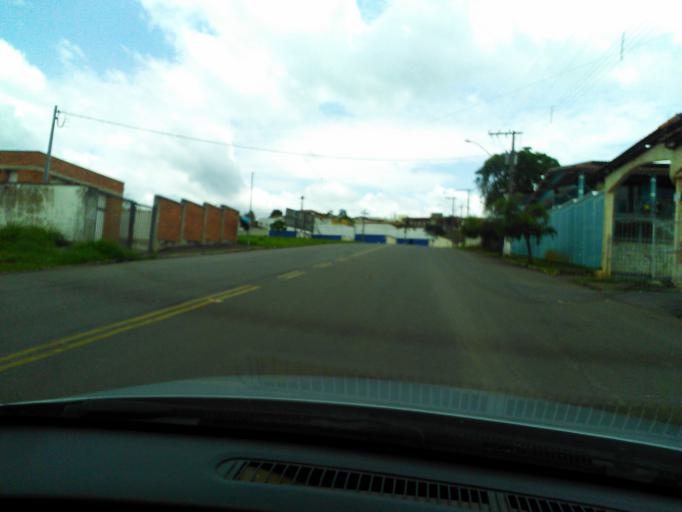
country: BR
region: Minas Gerais
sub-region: Tres Coracoes
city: Tres Coracoes
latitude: -21.6733
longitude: -45.2702
